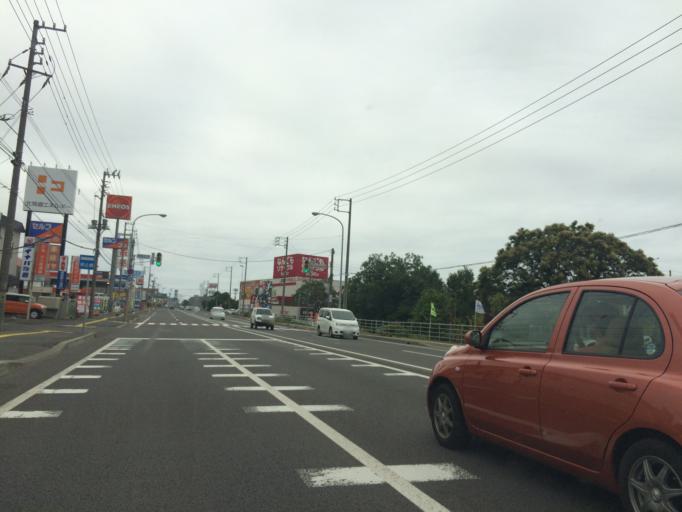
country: JP
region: Hokkaido
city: Sapporo
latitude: 43.1255
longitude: 141.2198
